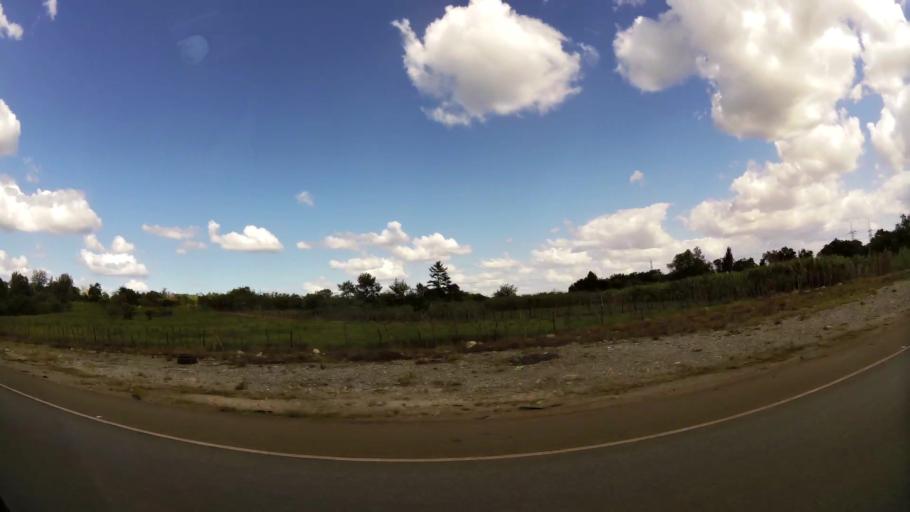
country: DO
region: Santo Domingo
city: Santo Domingo Oeste
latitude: 18.5435
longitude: -70.0793
